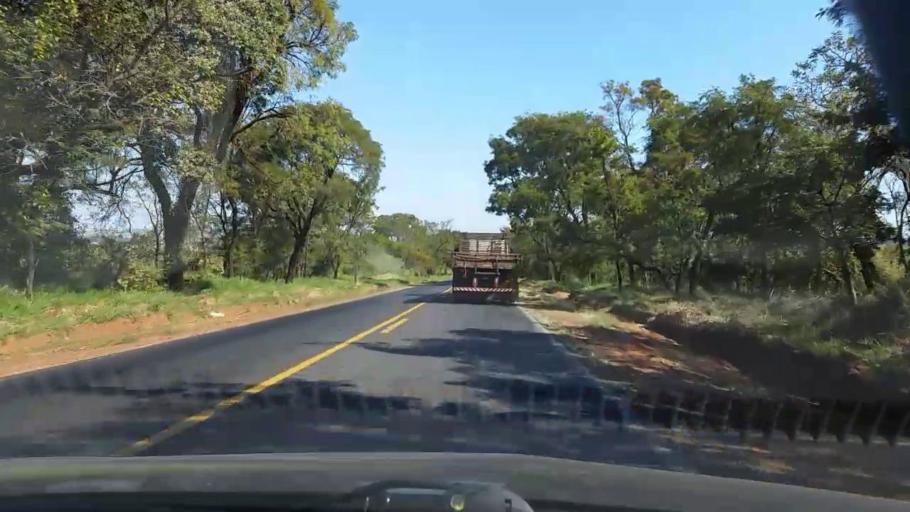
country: BR
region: Sao Paulo
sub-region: Sao Manuel
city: Sao Manuel
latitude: -22.7924
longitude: -48.6558
